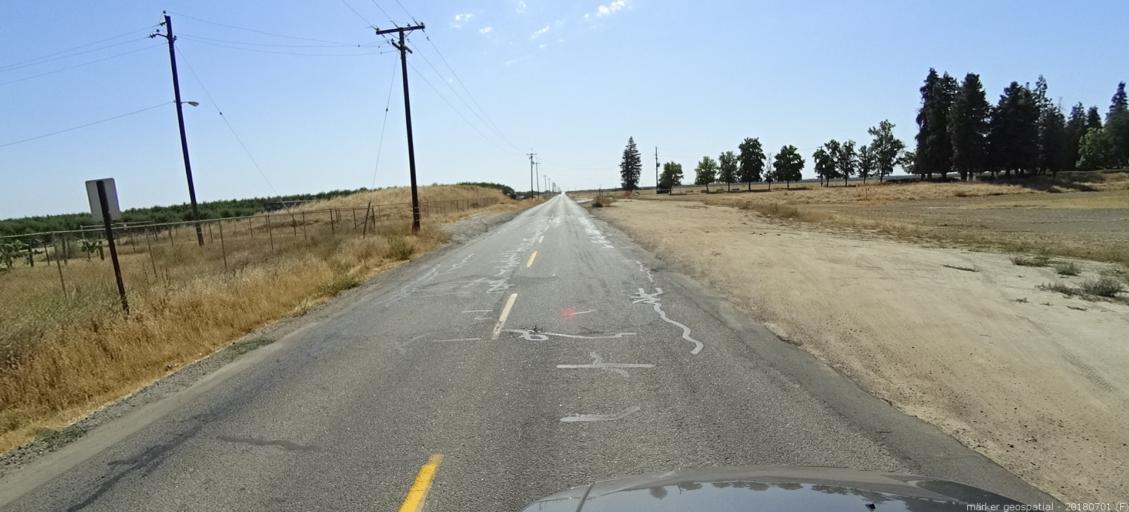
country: US
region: California
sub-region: Madera County
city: Parksdale
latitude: 36.8802
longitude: -119.9717
